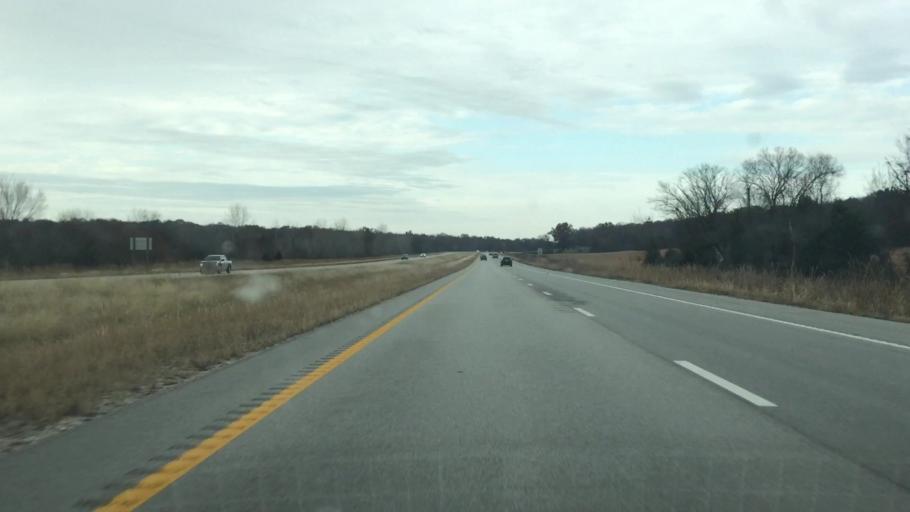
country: US
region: Missouri
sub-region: Henry County
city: Clinton
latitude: 38.2087
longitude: -93.7550
